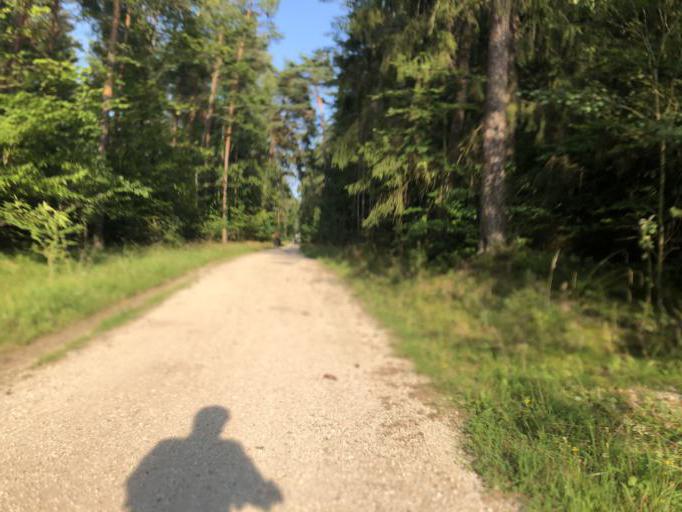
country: DE
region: Bavaria
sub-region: Regierungsbezirk Mittelfranken
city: Buckenhof
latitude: 49.5651
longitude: 11.0659
